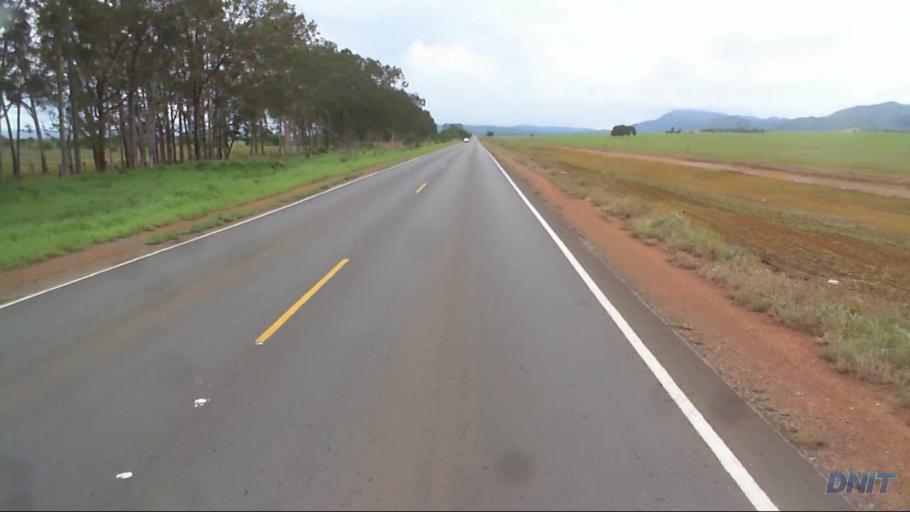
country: BR
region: Goias
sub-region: Padre Bernardo
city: Padre Bernardo
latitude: -15.3215
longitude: -48.2300
